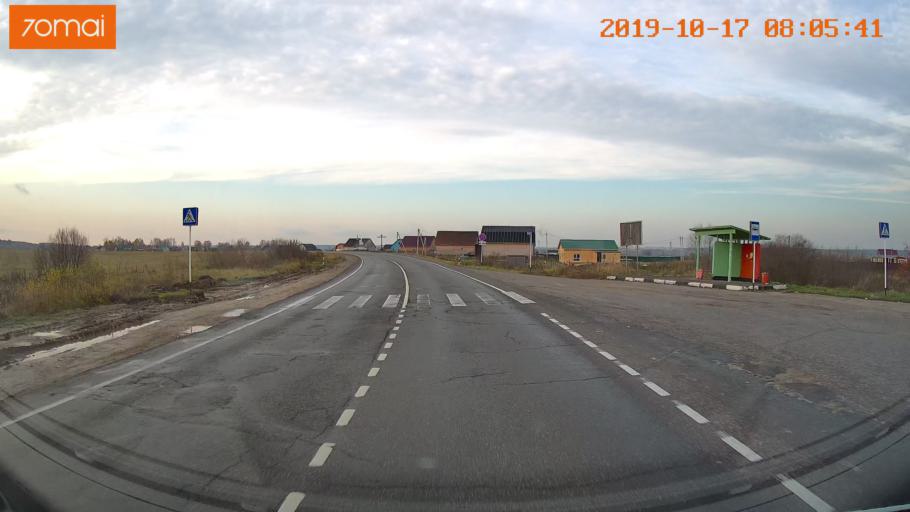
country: RU
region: Vladimir
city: Kol'chugino
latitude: 56.3321
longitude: 39.4112
